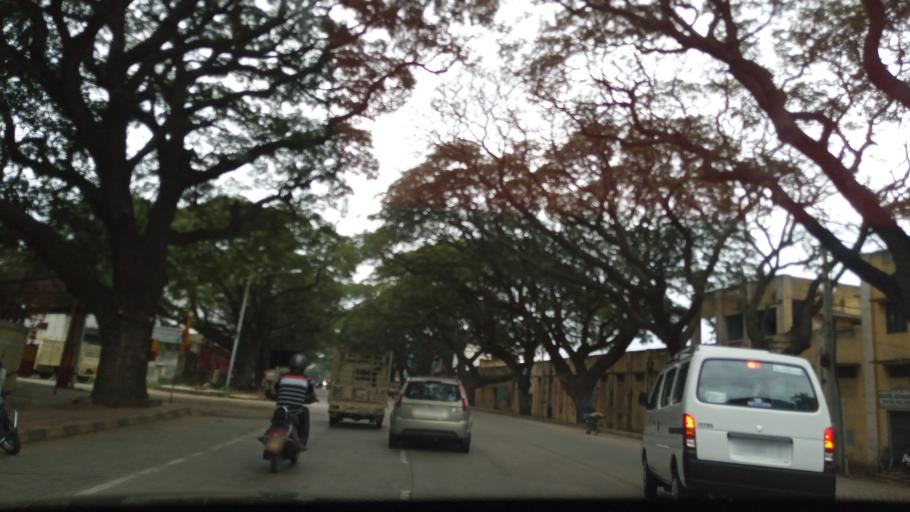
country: IN
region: Karnataka
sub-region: Mysore
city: Mysore
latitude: 12.3228
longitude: 76.6458
